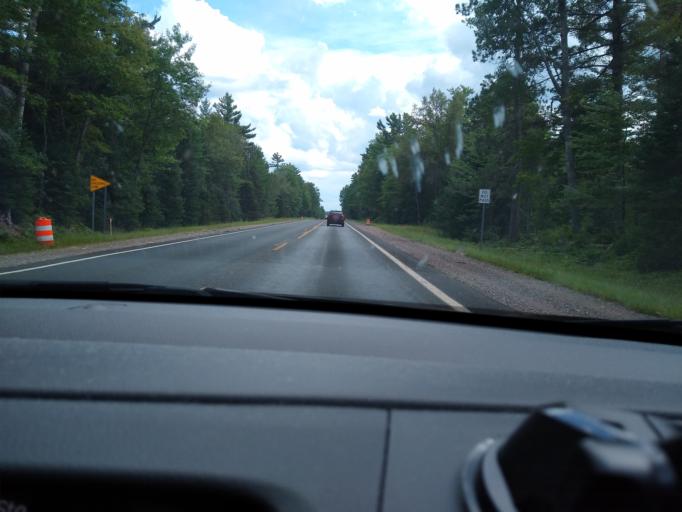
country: US
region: Michigan
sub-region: Iron County
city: Crystal Falls
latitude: 46.2561
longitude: -88.0125
